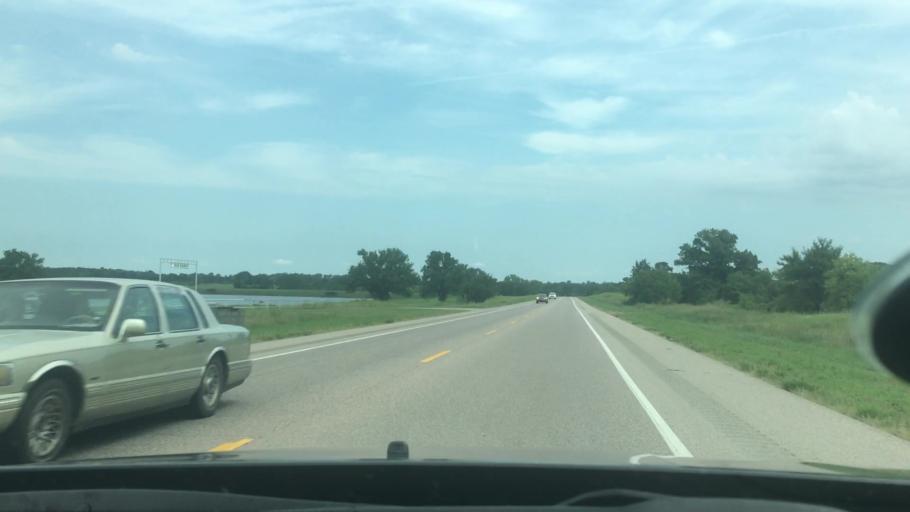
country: US
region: Oklahoma
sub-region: Seminole County
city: Seminole
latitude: 35.1662
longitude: -96.6742
